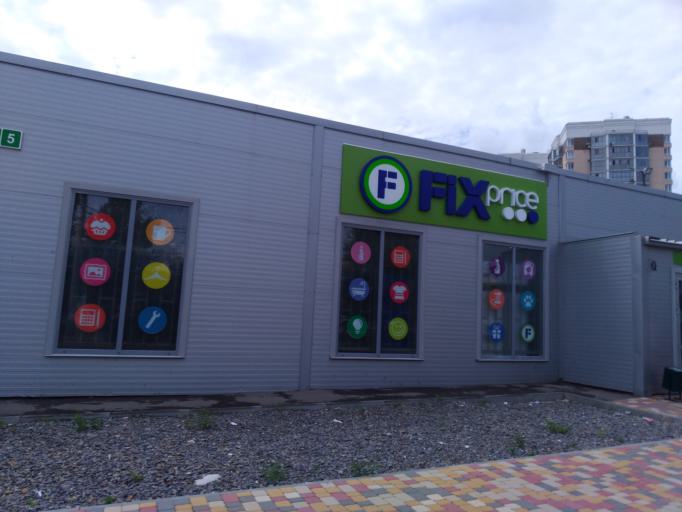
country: RU
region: Volgograd
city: Volgograd
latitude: 48.7141
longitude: 44.4955
